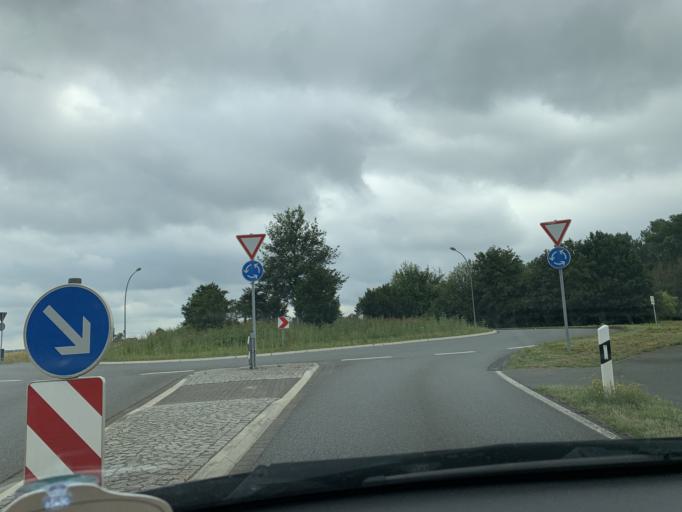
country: DE
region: North Rhine-Westphalia
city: Oelde
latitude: 51.8200
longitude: 8.1069
